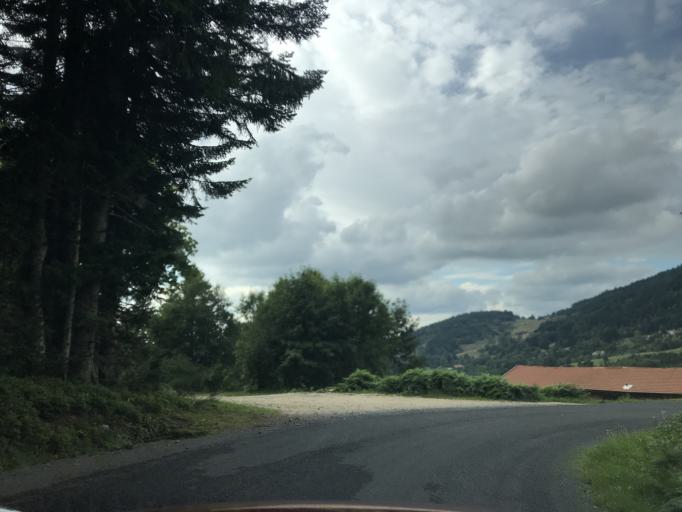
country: FR
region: Auvergne
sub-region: Departement du Puy-de-Dome
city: Job
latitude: 45.6631
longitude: 3.7641
